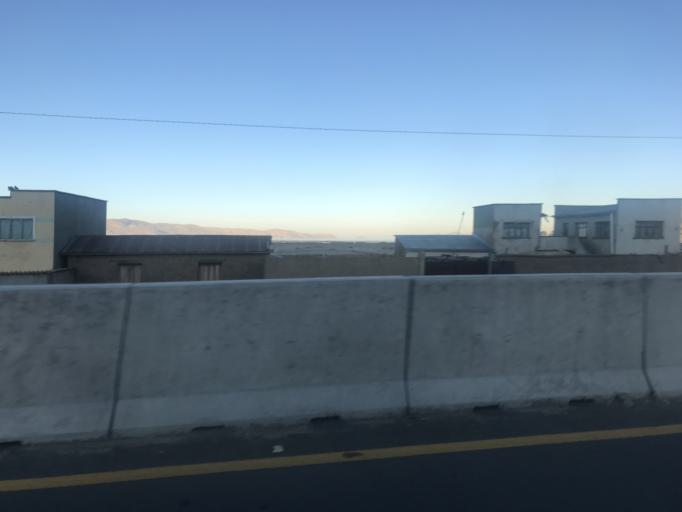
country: BO
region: La Paz
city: Batallas
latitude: -16.2441
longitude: -68.5722
